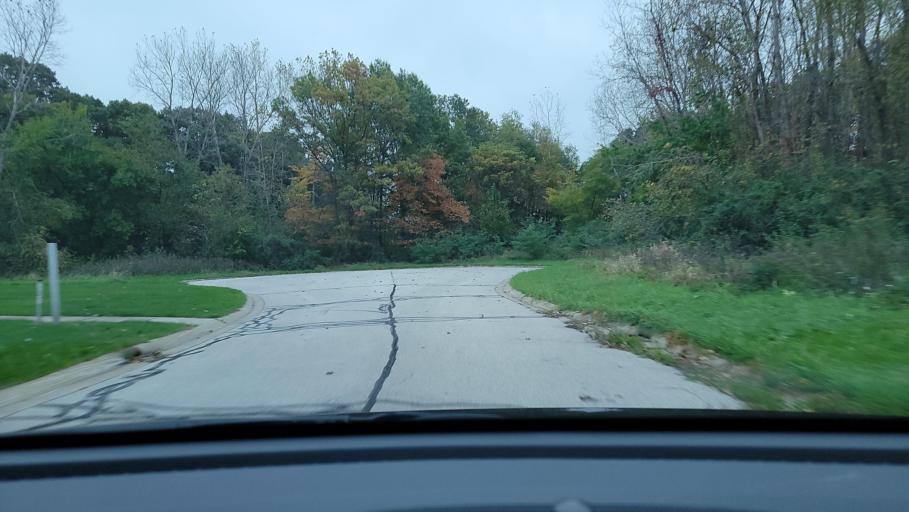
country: US
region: Indiana
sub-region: Porter County
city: Portage
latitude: 41.5657
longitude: -87.1794
